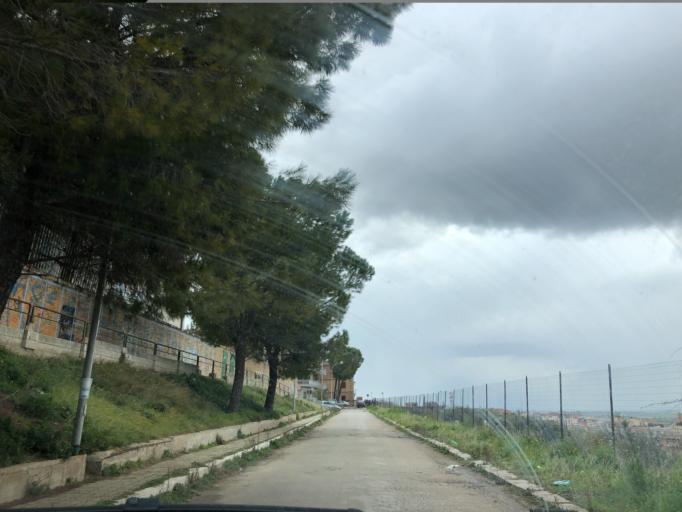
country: IT
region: Apulia
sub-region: Provincia di Foggia
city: Lucera
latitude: 41.5062
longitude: 15.3276
